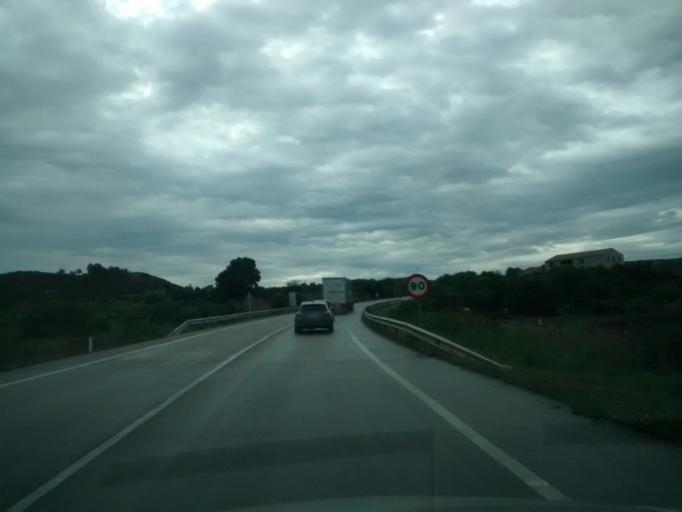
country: ES
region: Aragon
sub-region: Provincia de Zaragoza
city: Maella
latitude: 41.1304
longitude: 0.1275
